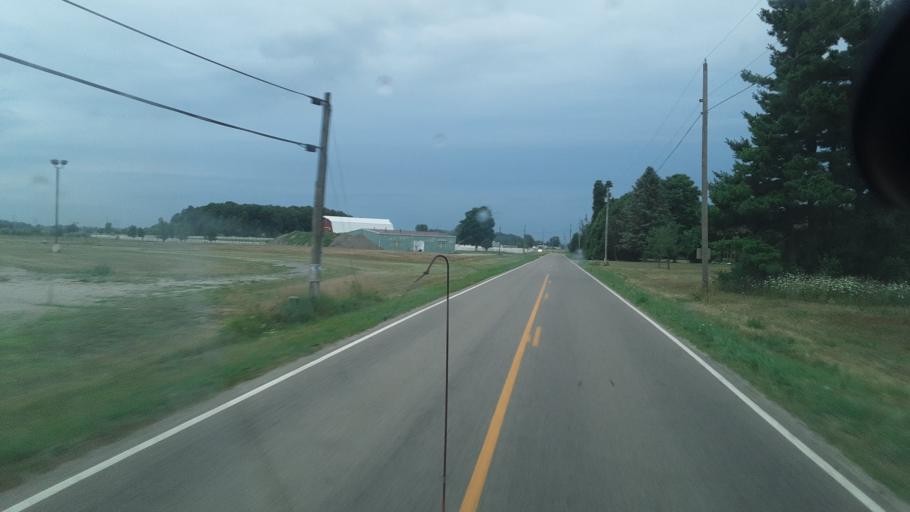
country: US
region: Ohio
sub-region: Defiance County
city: Hicksville
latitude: 41.2885
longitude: -84.7564
